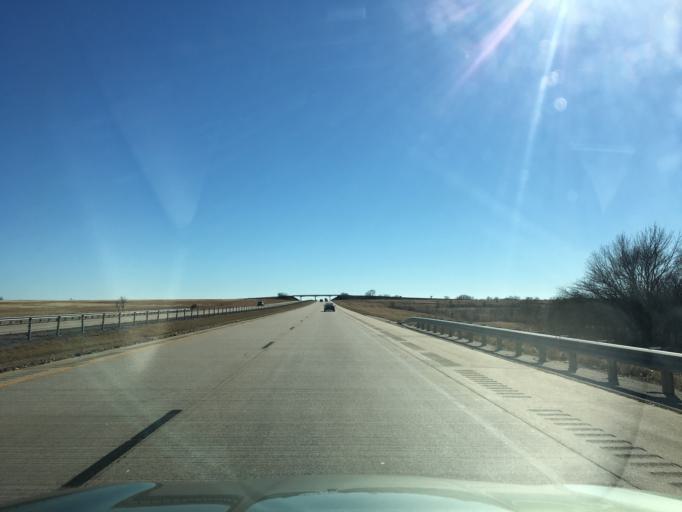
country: US
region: Oklahoma
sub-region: Kay County
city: Tonkawa
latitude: 36.4984
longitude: -97.3335
